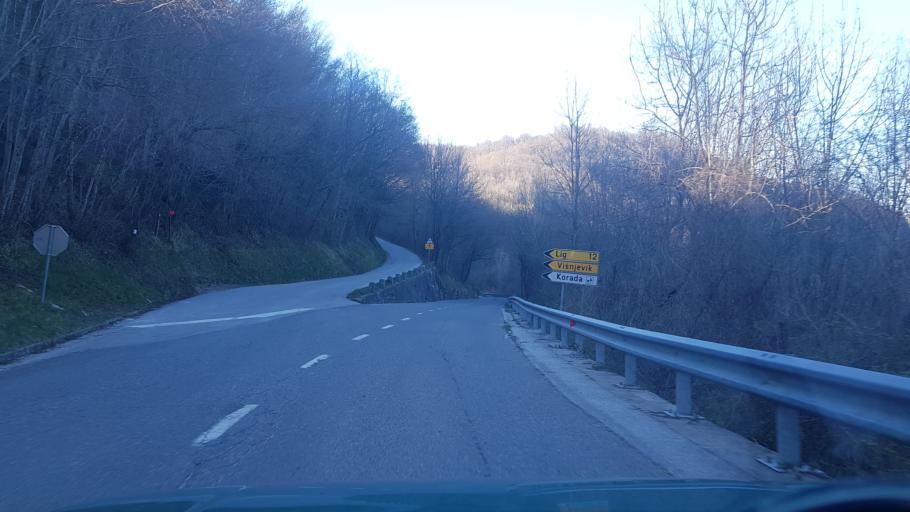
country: IT
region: Friuli Venezia Giulia
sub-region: Provincia di Gorizia
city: San Floriano del Collio
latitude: 46.0241
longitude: 13.5757
